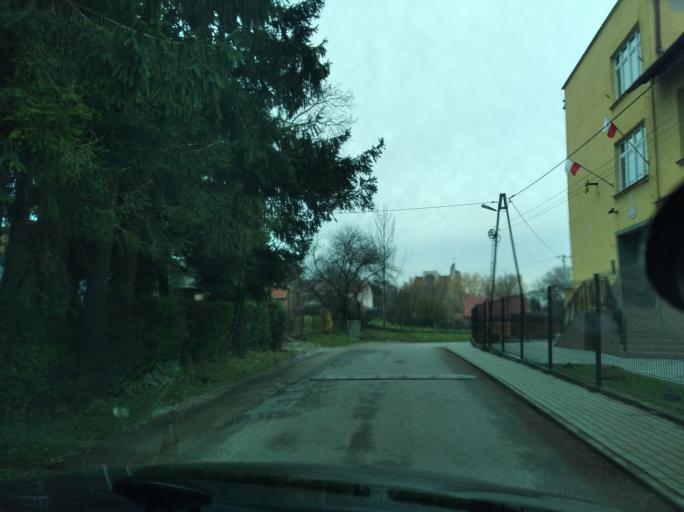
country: PL
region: Subcarpathian Voivodeship
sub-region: Powiat przeworski
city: Grzeska
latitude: 50.0748
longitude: 22.4545
